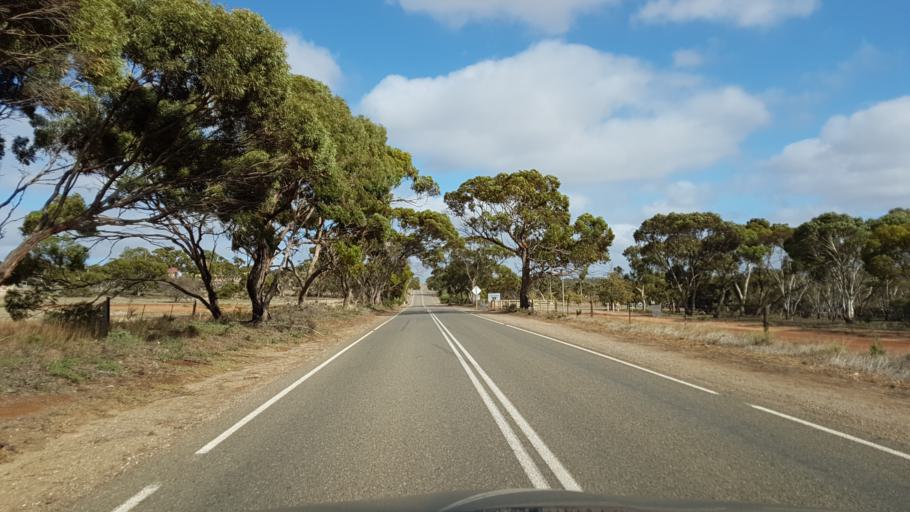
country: AU
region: South Australia
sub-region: Murray Bridge
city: Murray Bridge
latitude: -35.1175
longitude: 139.2355
